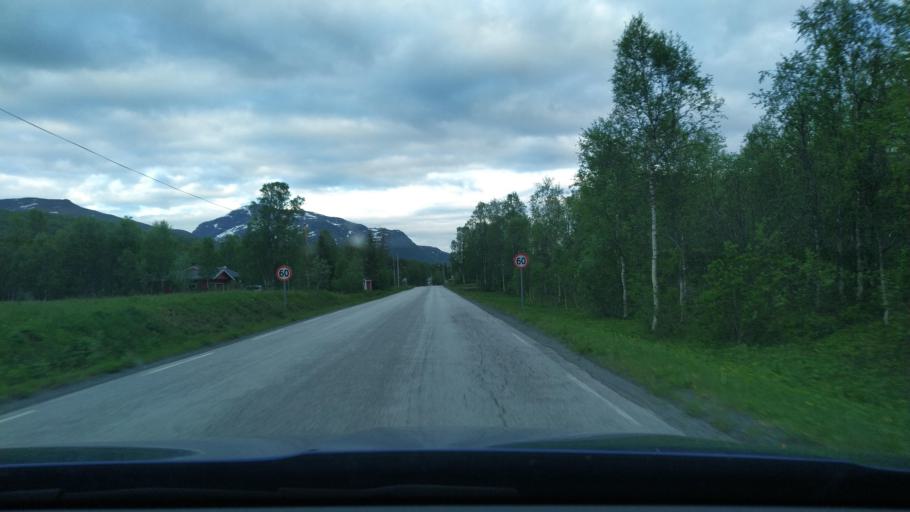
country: NO
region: Troms
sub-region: Dyroy
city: Brostadbotn
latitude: 69.0651
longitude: 17.7357
